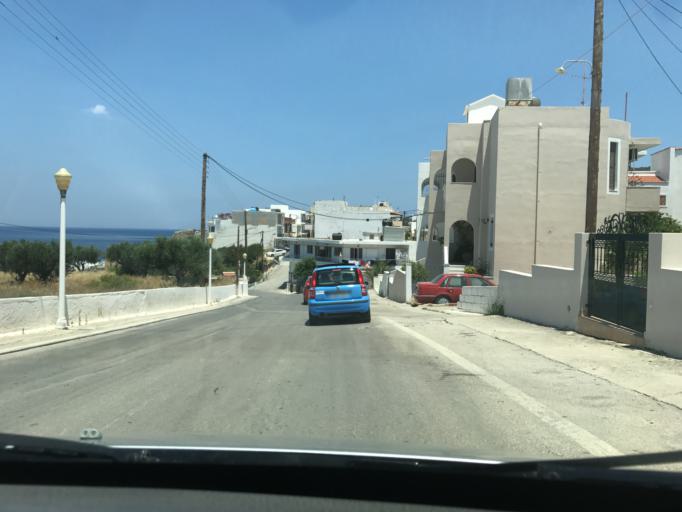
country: GR
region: South Aegean
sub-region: Nomos Dodekanisou
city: Karpathos
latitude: 35.5033
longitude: 27.2115
